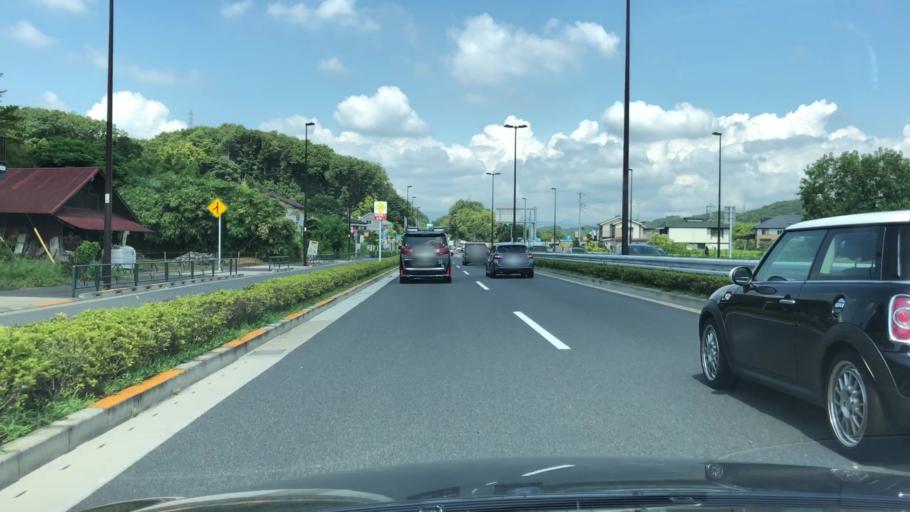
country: JP
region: Tokyo
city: Fussa
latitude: 35.6967
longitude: 139.3204
